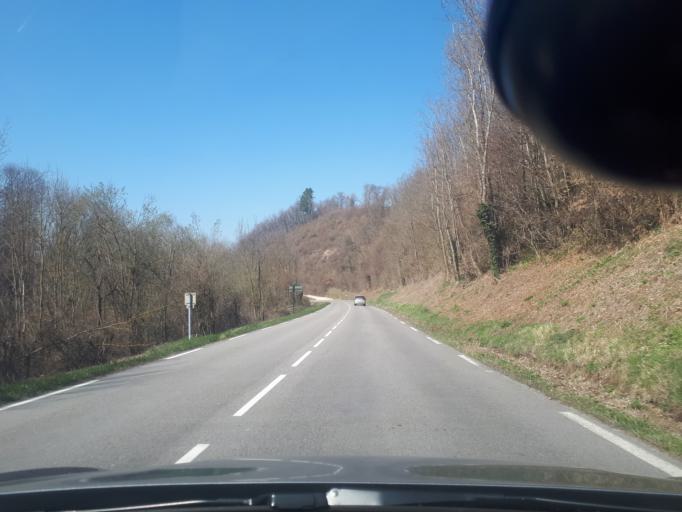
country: FR
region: Rhone-Alpes
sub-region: Departement de l'Isere
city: Nivolas-Vermelle
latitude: 45.5283
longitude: 5.3271
